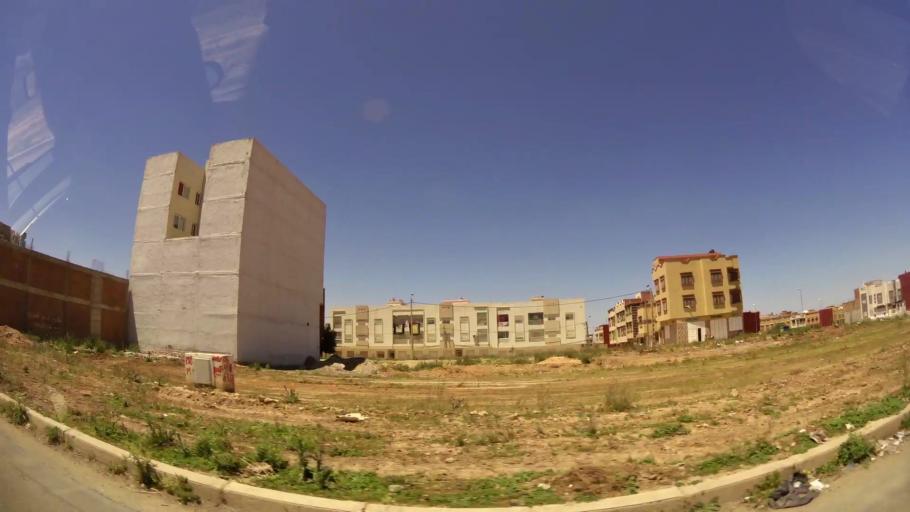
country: MA
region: Oriental
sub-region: Oujda-Angad
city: Oujda
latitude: 34.6708
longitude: -1.8757
